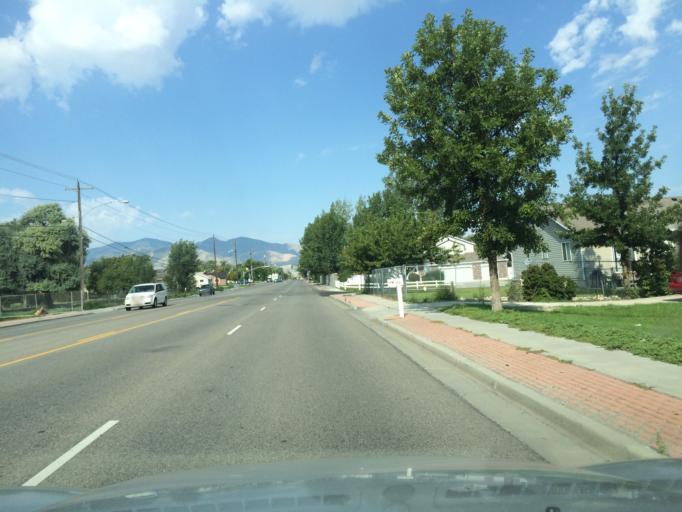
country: US
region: Utah
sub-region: Salt Lake County
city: West Valley City
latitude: 40.6966
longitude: -112.0124
